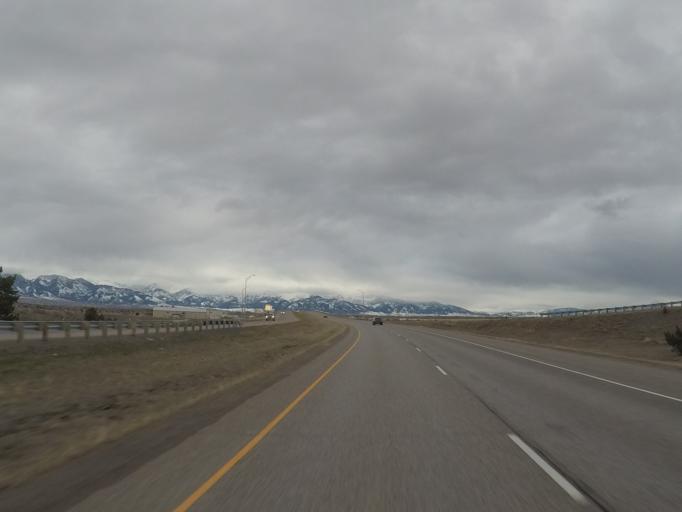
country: US
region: Montana
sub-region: Gallatin County
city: Manhattan
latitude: 45.8496
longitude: -111.3380
